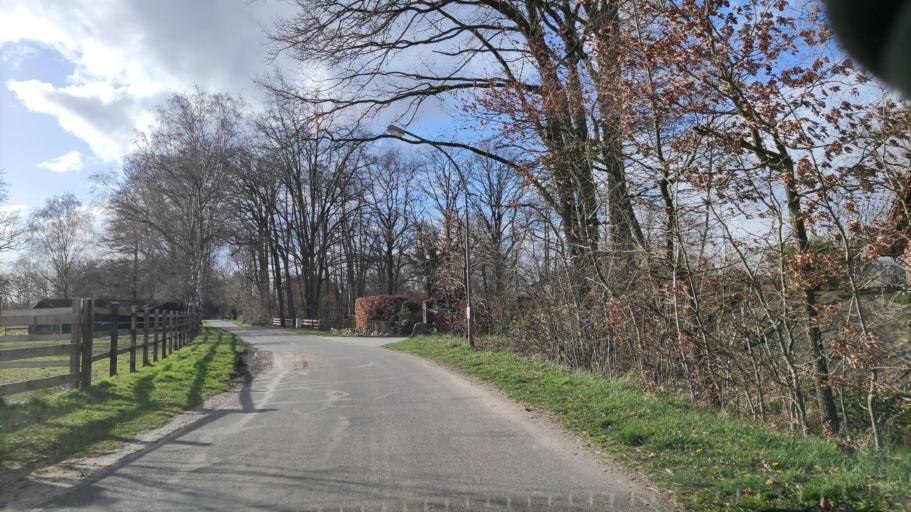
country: DE
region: Lower Saxony
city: Bienenbuttel
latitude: 53.1308
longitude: 10.5146
